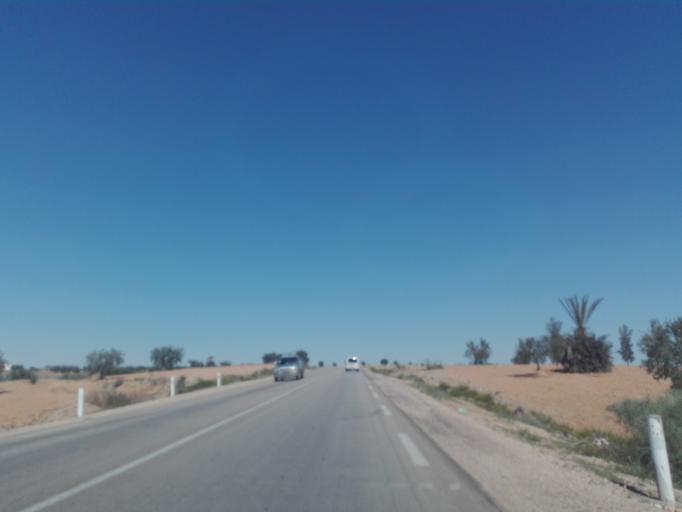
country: TN
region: Safaqis
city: Bi'r `Ali Bin Khalifah
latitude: 34.7452
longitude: 10.3625
